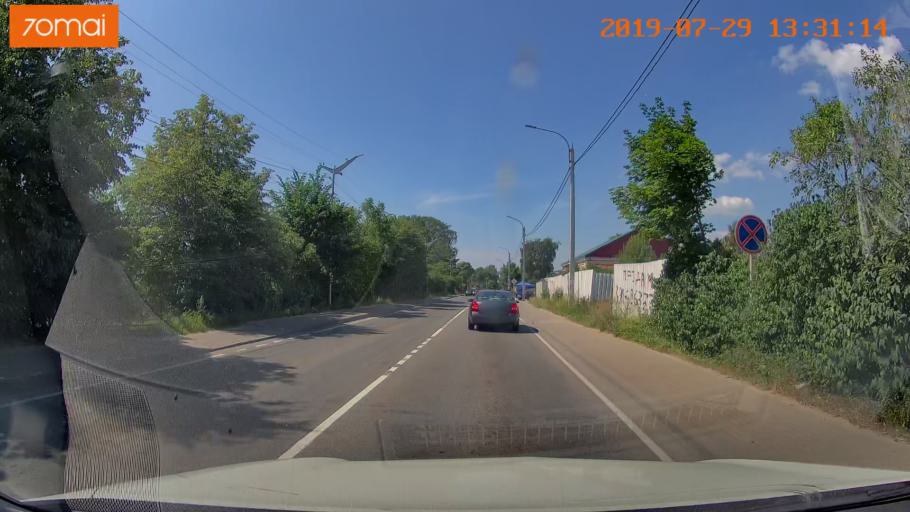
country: RU
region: Kaliningrad
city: Vzmorye
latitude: 54.6976
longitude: 20.2488
